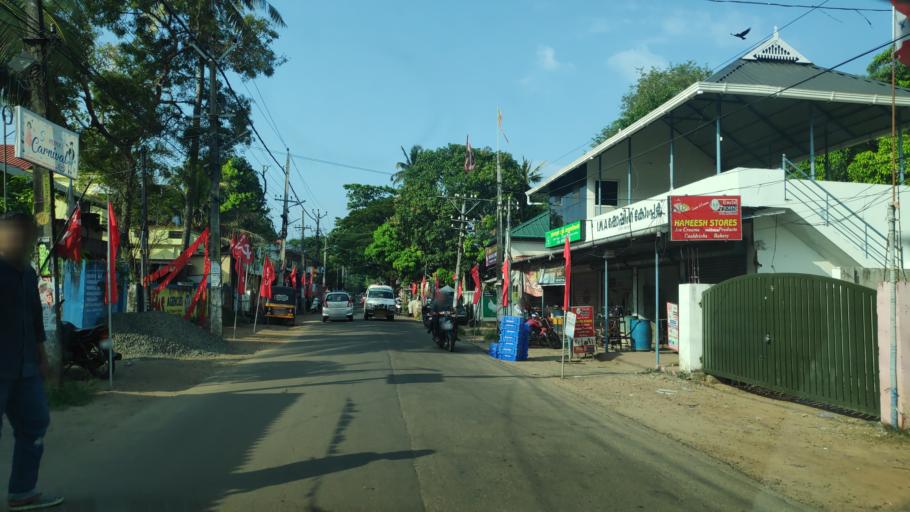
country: IN
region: Kerala
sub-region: Alappuzha
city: Alleppey
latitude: 9.4853
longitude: 76.3339
